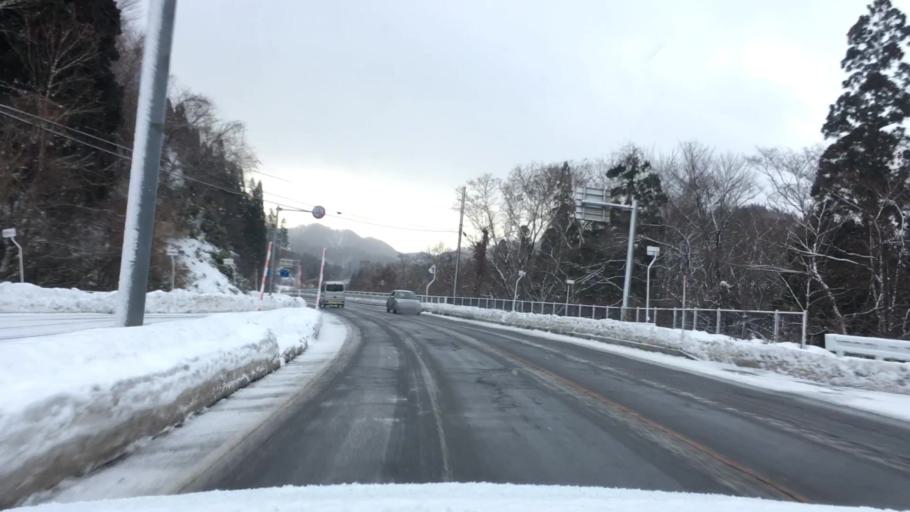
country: JP
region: Akita
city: Odate
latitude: 40.4451
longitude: 140.6341
